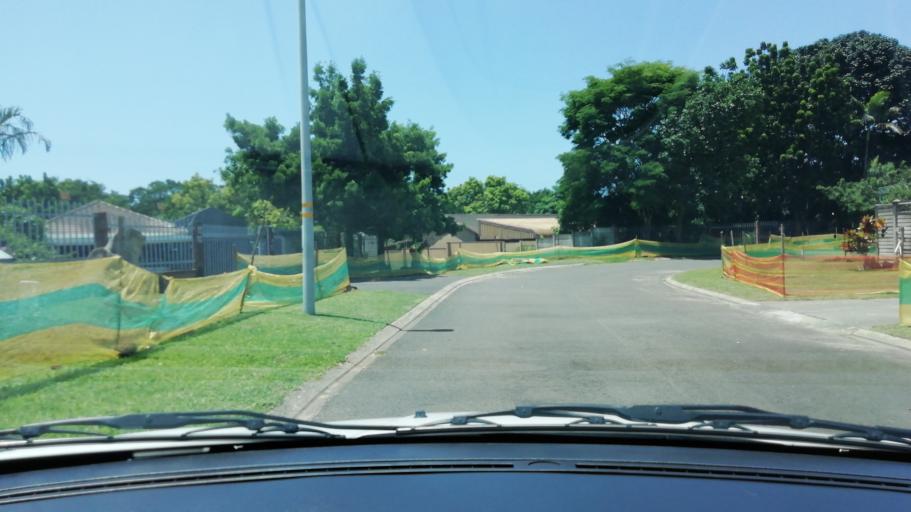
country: ZA
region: KwaZulu-Natal
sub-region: uThungulu District Municipality
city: Richards Bay
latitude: -28.7334
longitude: 32.0606
